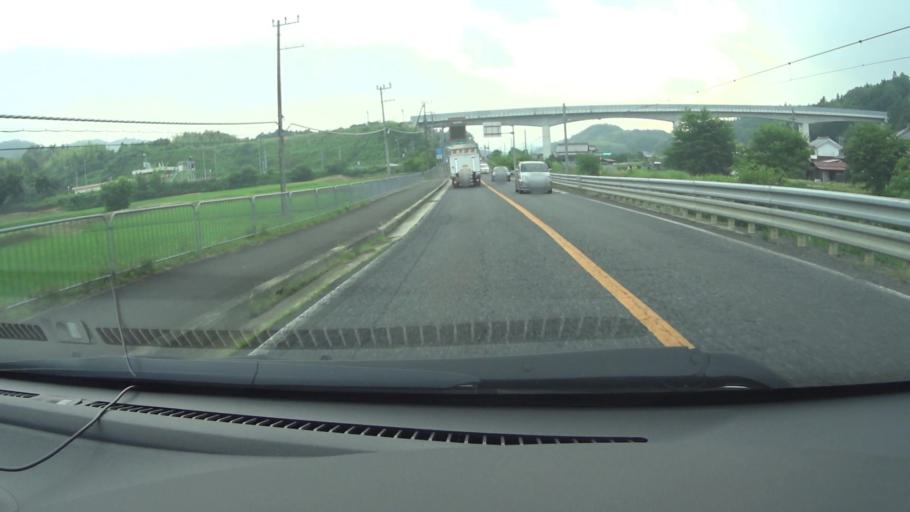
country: JP
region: Kyoto
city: Ayabe
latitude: 35.3401
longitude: 135.3096
